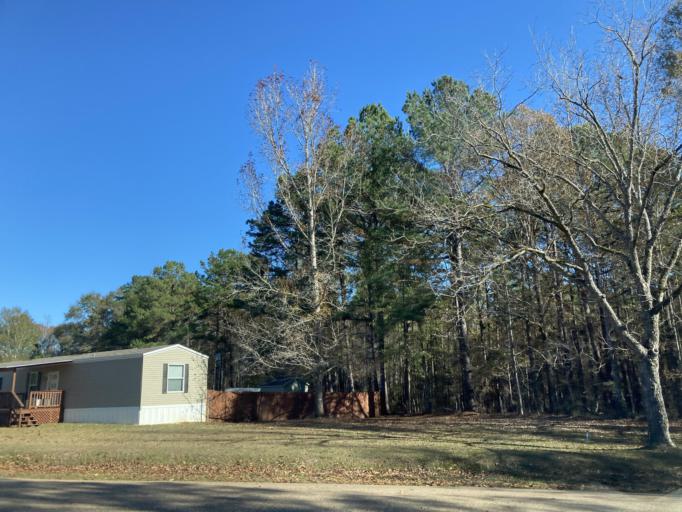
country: US
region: Mississippi
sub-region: Lamar County
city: Sumrall
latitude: 31.2632
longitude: -89.5274
